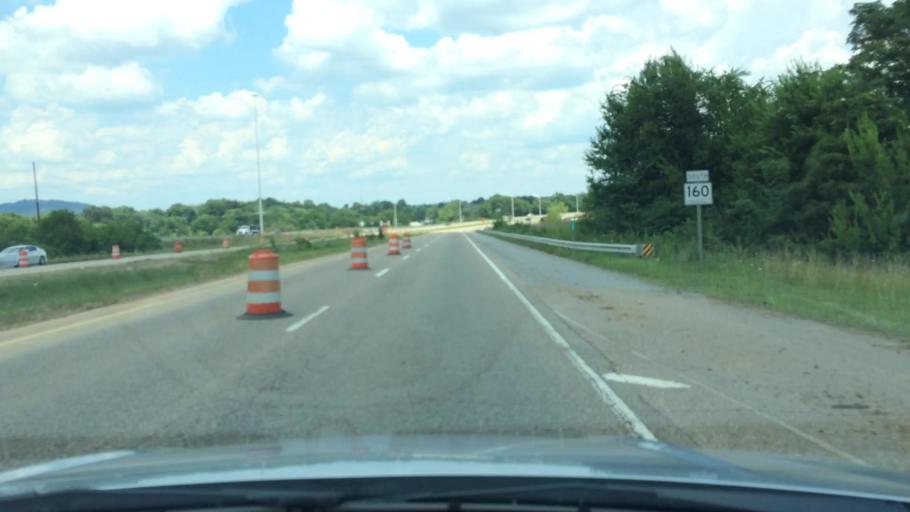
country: US
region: Tennessee
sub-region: Hamblen County
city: Morristown
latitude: 36.1756
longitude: -83.3461
